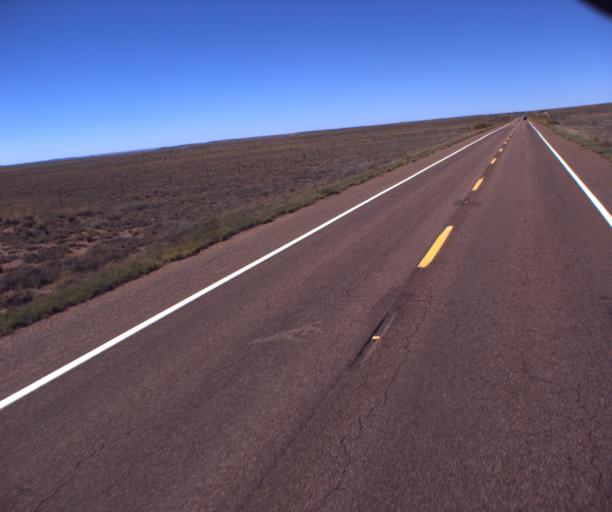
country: US
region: Arizona
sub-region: Navajo County
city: Holbrook
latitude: 34.7850
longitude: -109.8670
